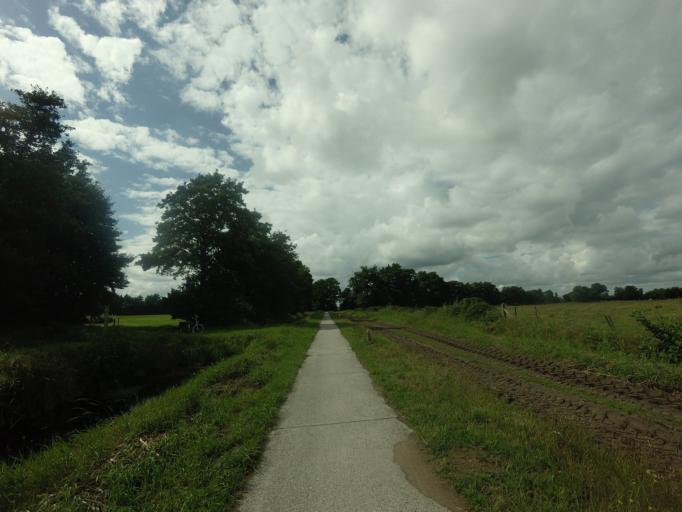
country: NL
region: Overijssel
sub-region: Gemeente Steenwijkerland
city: Wanneperveen
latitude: 52.7066
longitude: 6.1114
